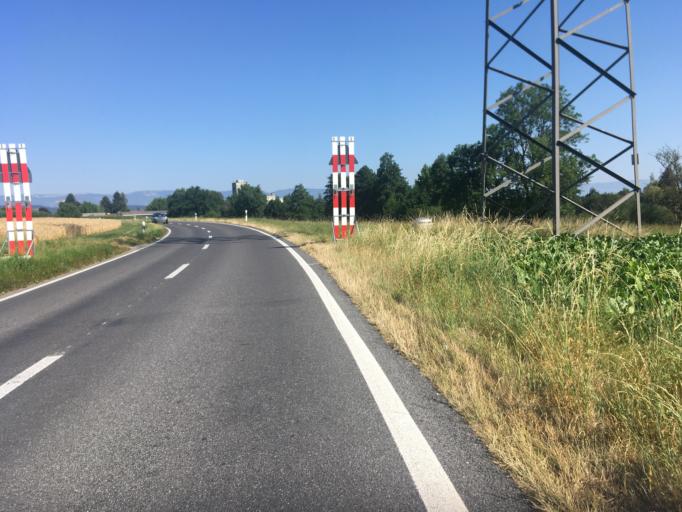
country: CH
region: Bern
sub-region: Bern-Mittelland District
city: Fraubrunnen
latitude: 47.0806
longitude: 7.5297
